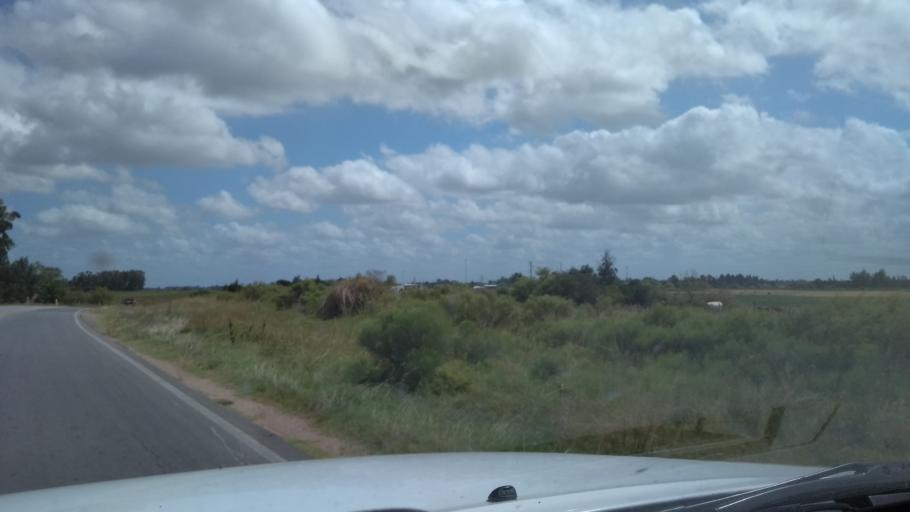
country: UY
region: Canelones
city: Santa Rosa
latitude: -34.4870
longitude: -56.0131
